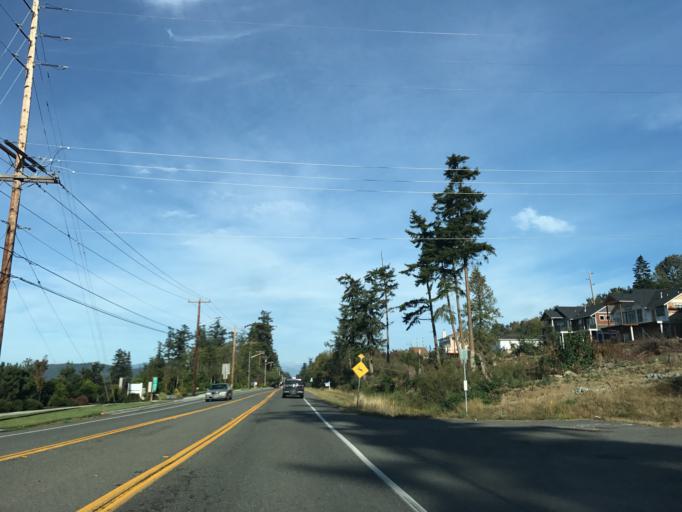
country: US
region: Washington
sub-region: Skagit County
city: Anacortes
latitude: 48.5072
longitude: -122.6570
